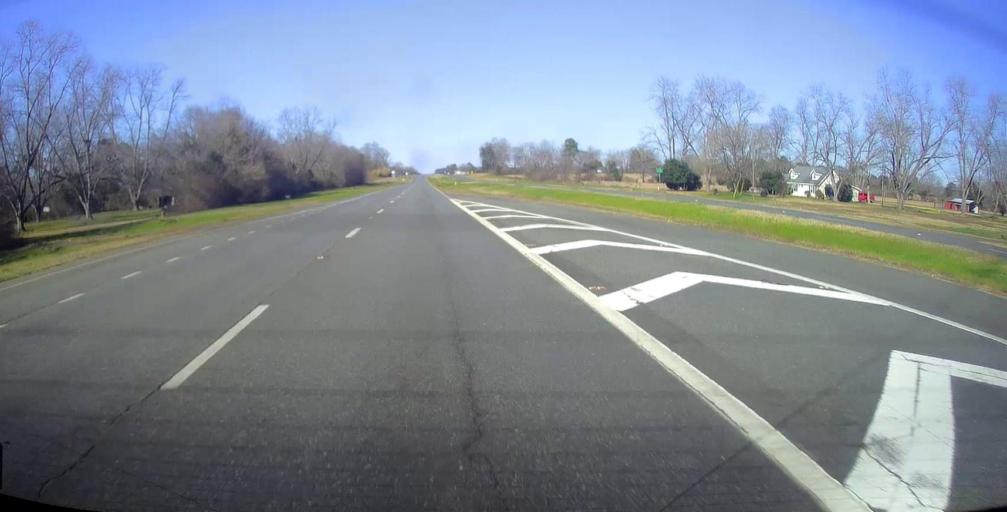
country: US
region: Georgia
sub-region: Schley County
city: Ellaville
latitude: 32.1603
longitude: -84.2702
